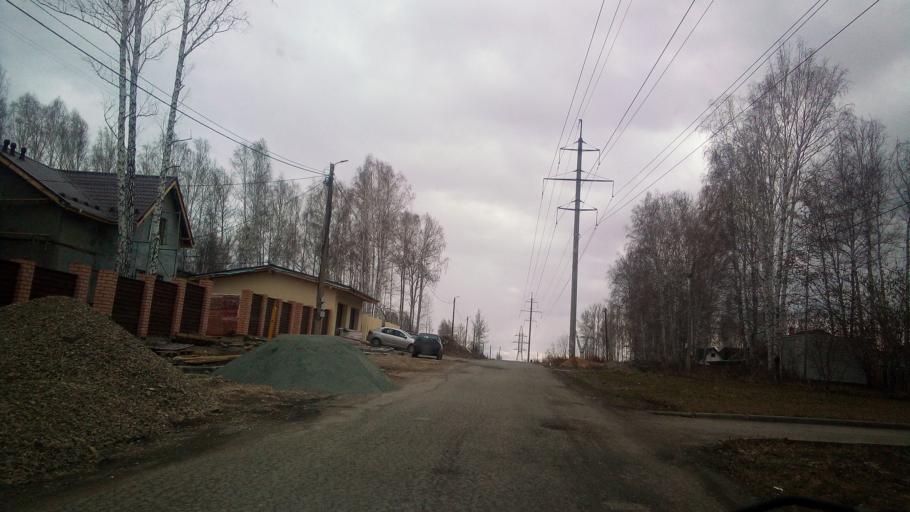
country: RU
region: Chelyabinsk
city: Sargazy
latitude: 55.1313
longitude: 61.2432
